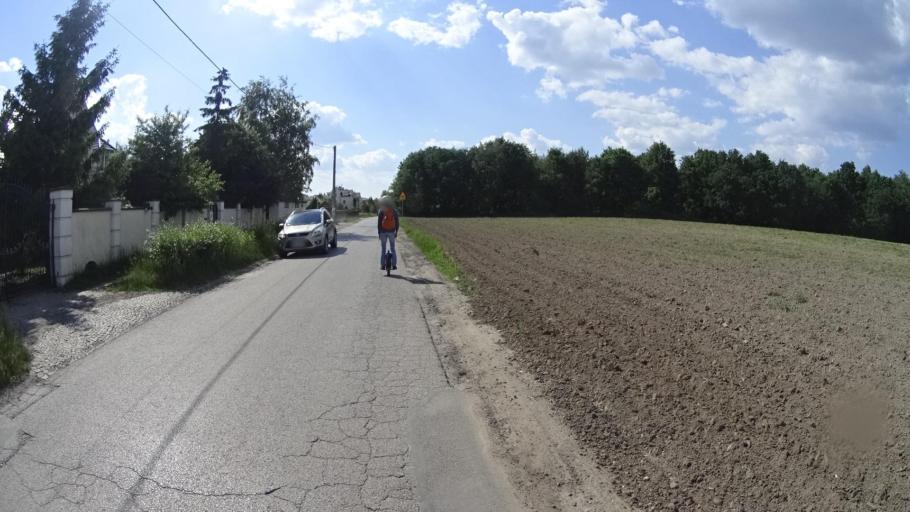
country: PL
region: Masovian Voivodeship
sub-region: Powiat piaseczynski
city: Jozefoslaw
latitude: 52.1062
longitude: 21.0541
